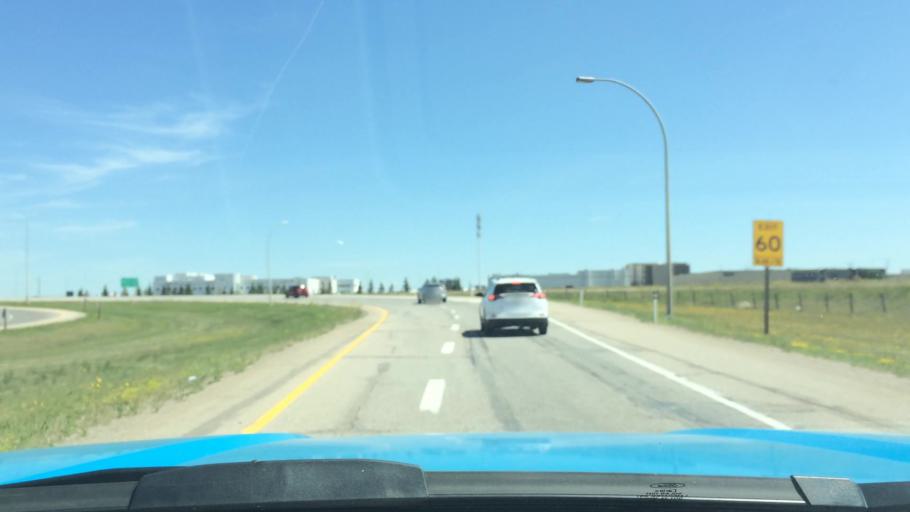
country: CA
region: Alberta
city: Calgary
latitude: 51.1525
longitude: -114.0177
